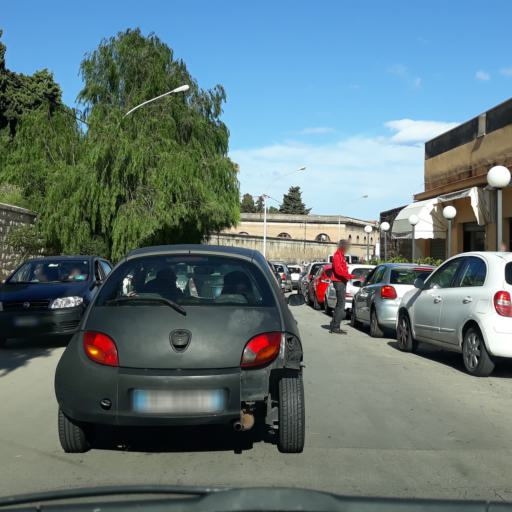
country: IT
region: Sicily
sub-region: Palermo
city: Palermo
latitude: 38.1583
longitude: 13.3710
